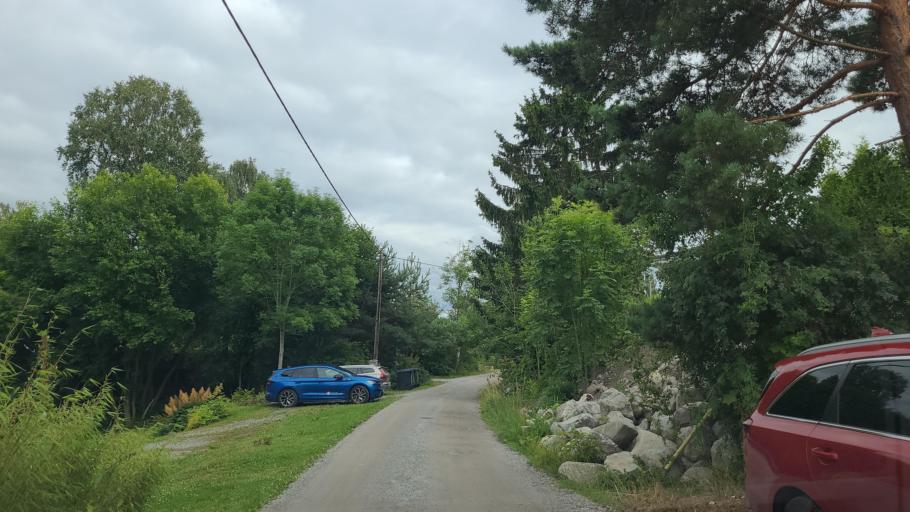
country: SE
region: Stockholm
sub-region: Upplands-Bro Kommun
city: Bro
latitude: 59.4770
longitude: 17.5572
